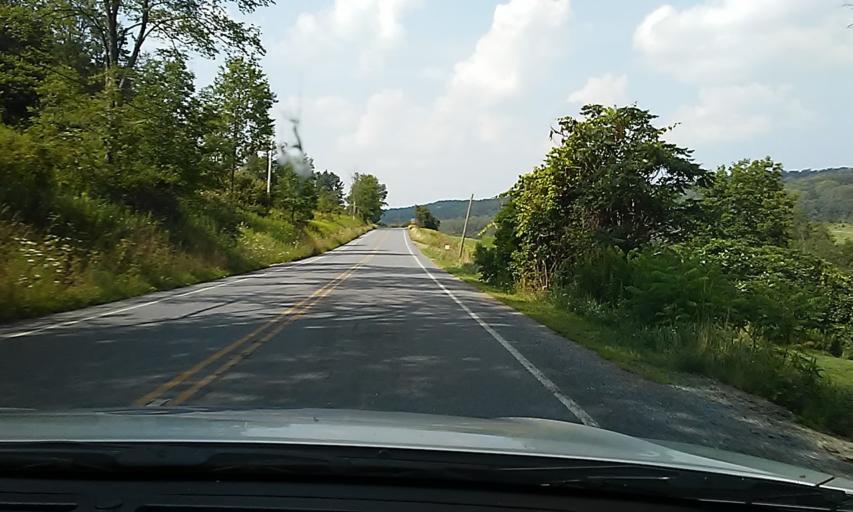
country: US
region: New York
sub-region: Allegany County
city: Wellsville
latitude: 41.9339
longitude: -77.8523
